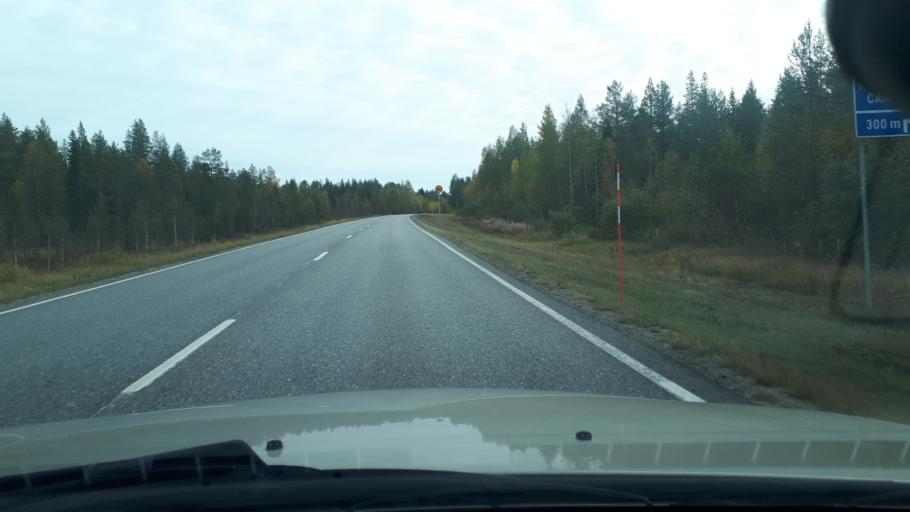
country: FI
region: Lapland
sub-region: Rovaniemi
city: Ranua
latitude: 65.9463
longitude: 26.4529
